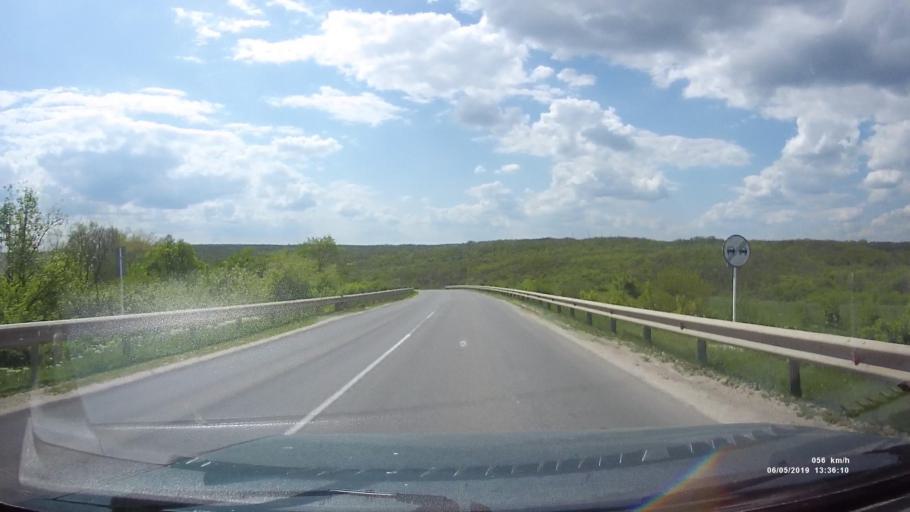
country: RU
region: Rostov
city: Ust'-Donetskiy
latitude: 47.6918
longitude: 40.7361
